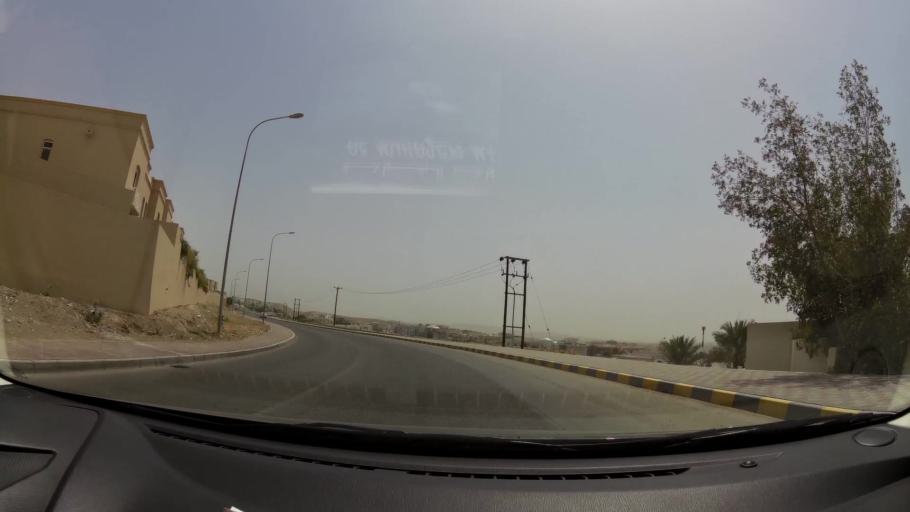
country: OM
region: Muhafazat Masqat
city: Bawshar
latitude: 23.5611
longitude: 58.4004
